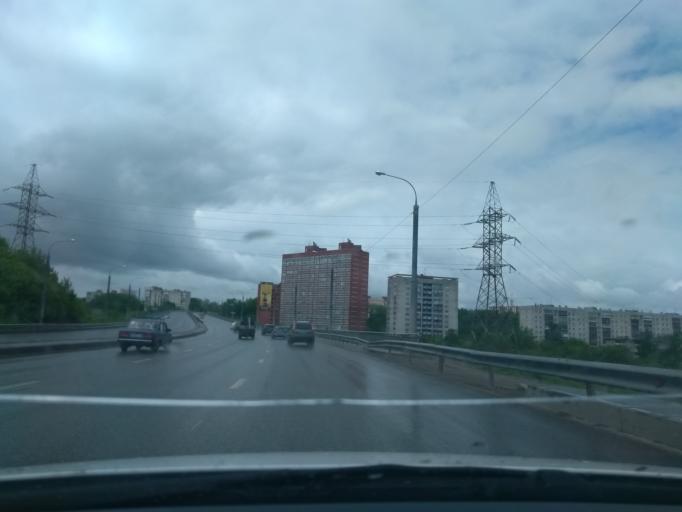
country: RU
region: Perm
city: Perm
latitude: 57.9861
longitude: 56.2359
